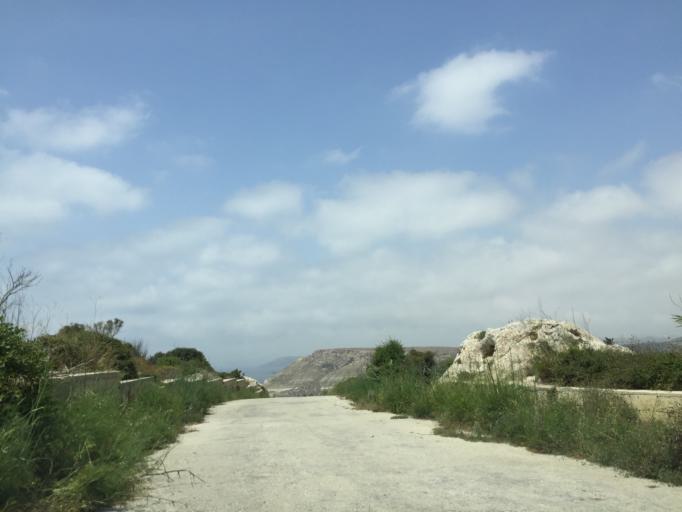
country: MT
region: L-Imgarr
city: Imgarr
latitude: 35.9013
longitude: 14.3368
